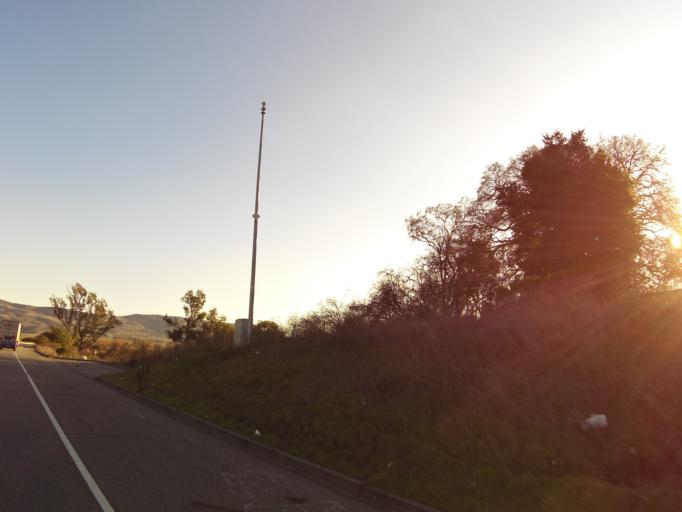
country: US
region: California
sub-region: Santa Clara County
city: Gilroy
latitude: 36.9307
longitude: -121.5493
